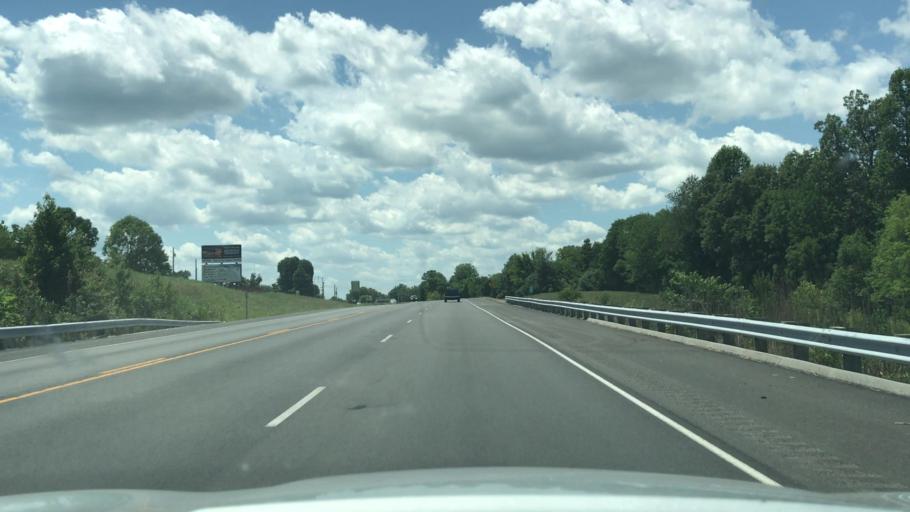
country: US
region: Kentucky
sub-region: Muhlenberg County
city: Greenville
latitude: 37.2023
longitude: -87.2013
